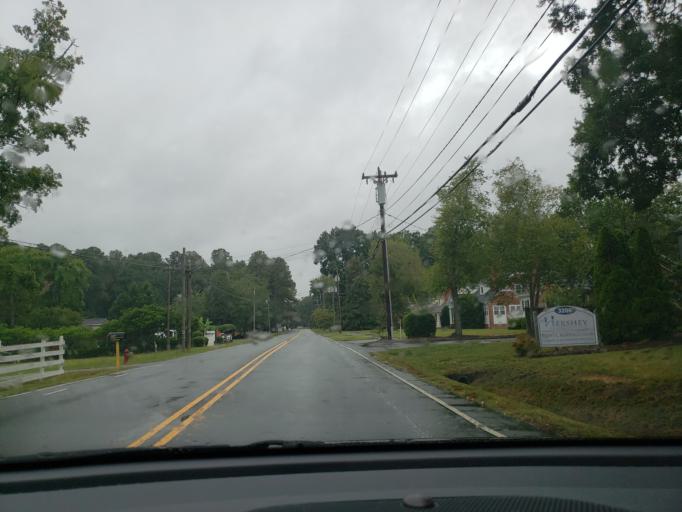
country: US
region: North Carolina
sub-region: Durham County
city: Durham
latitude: 35.9667
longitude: -78.9460
